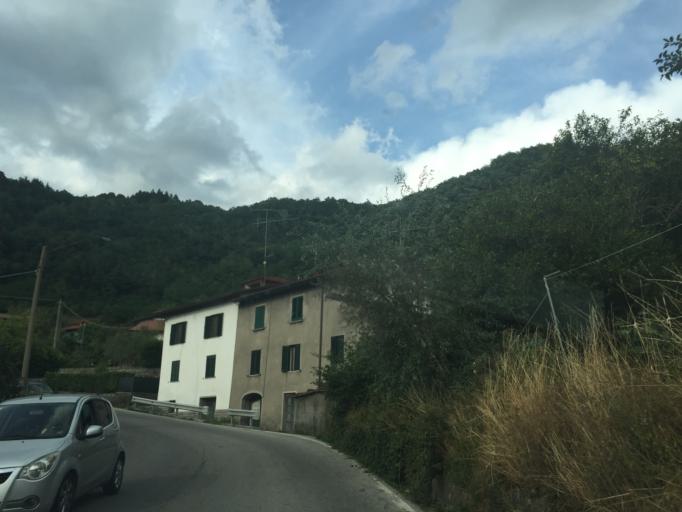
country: IT
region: Tuscany
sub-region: Provincia di Pistoia
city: San Marcello Pistoiese
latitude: 44.0565
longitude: 10.7740
